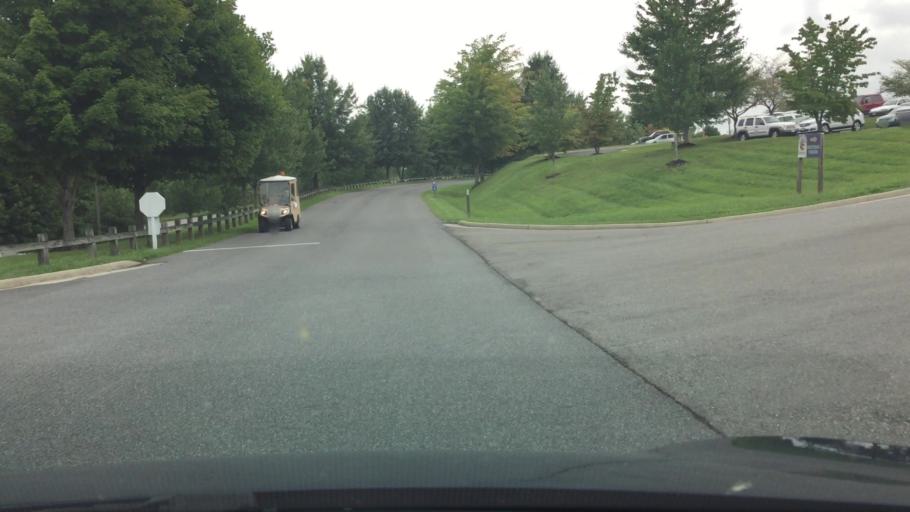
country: US
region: Virginia
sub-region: City of Radford
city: Radford
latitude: 37.0889
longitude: -80.5069
